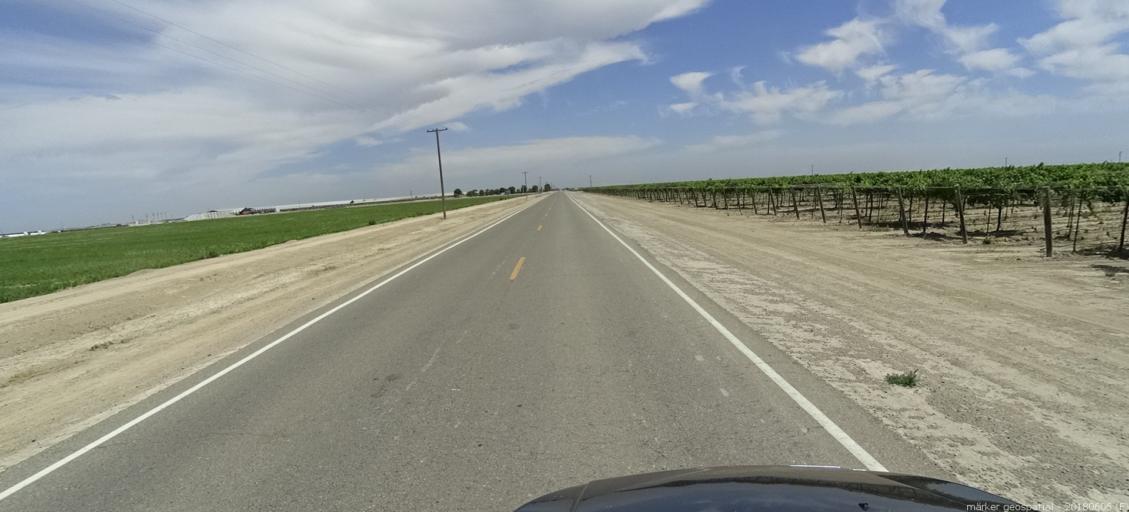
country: US
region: California
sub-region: Fresno County
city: Firebaugh
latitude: 36.9273
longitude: -120.3822
